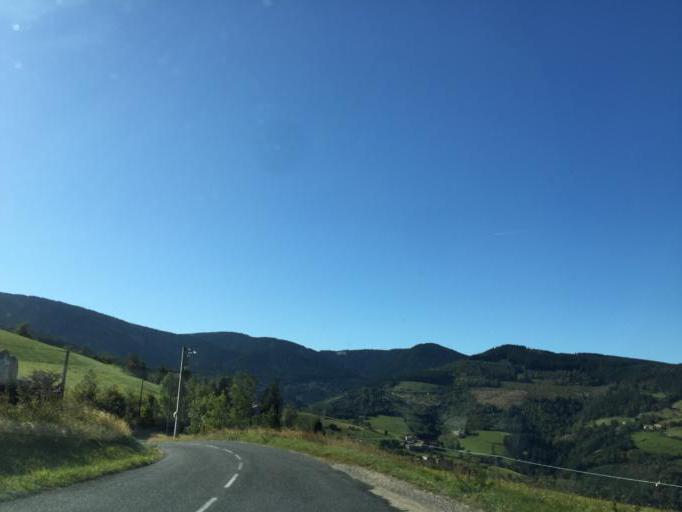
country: FR
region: Rhone-Alpes
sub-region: Departement de la Loire
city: Saint-Chamond
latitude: 45.4157
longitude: 4.5486
